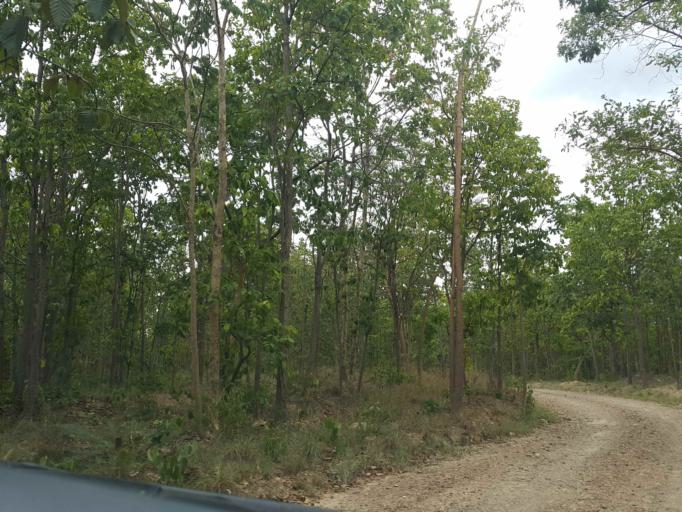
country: TH
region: Chiang Mai
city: Doi Lo
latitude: 18.5086
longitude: 98.7413
